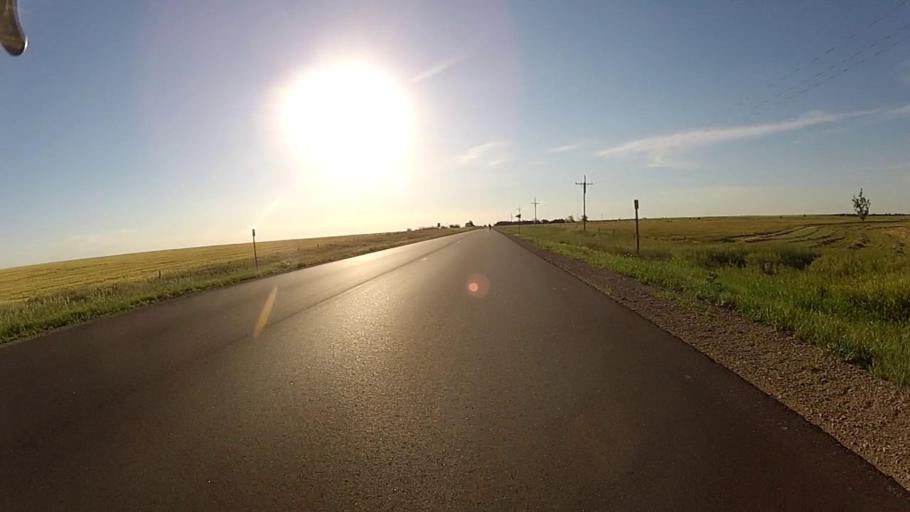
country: US
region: Kansas
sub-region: Comanche County
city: Coldwater
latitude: 37.2817
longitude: -99.1588
